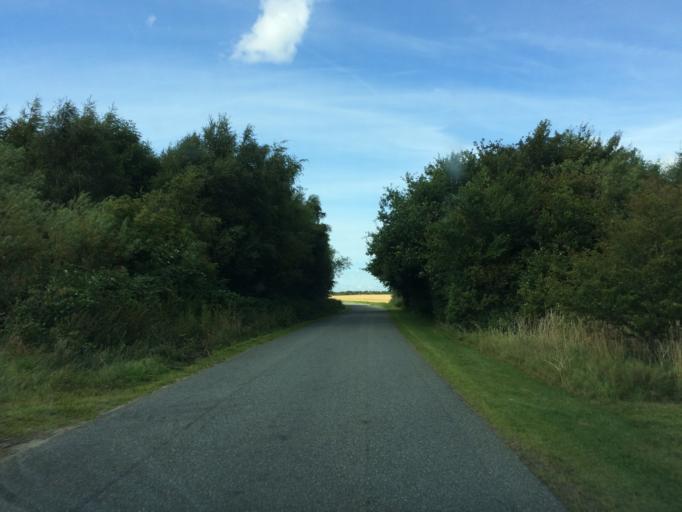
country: DK
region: Central Jutland
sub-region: Ringkobing-Skjern Kommune
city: Skjern
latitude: 56.0216
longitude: 8.4063
